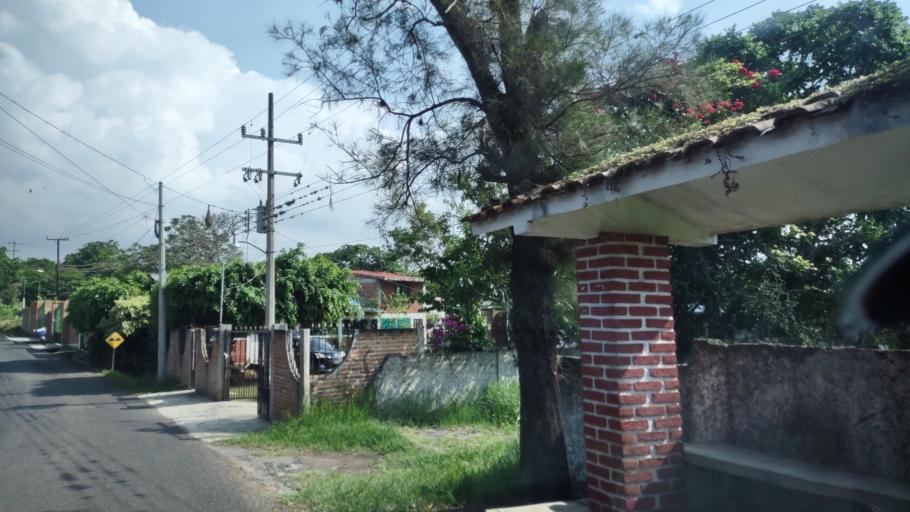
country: MX
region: Veracruz
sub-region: Coatepec
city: Bella Esperanza
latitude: 19.4542
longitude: -96.8321
